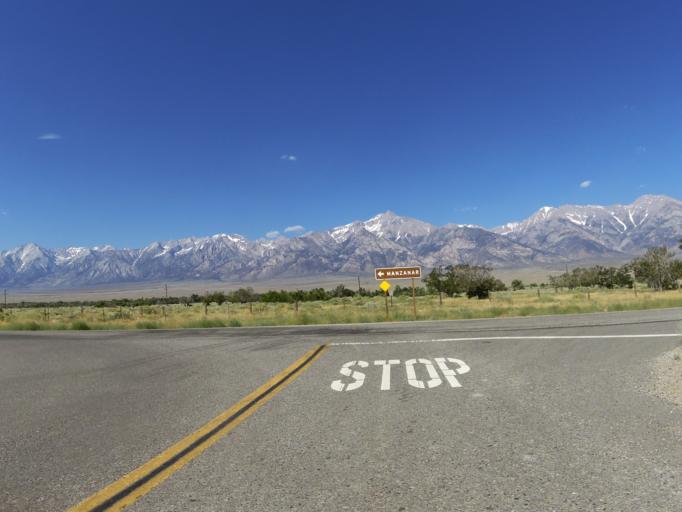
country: US
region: California
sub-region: Inyo County
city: Lone Pine
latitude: 36.7344
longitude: -118.1498
